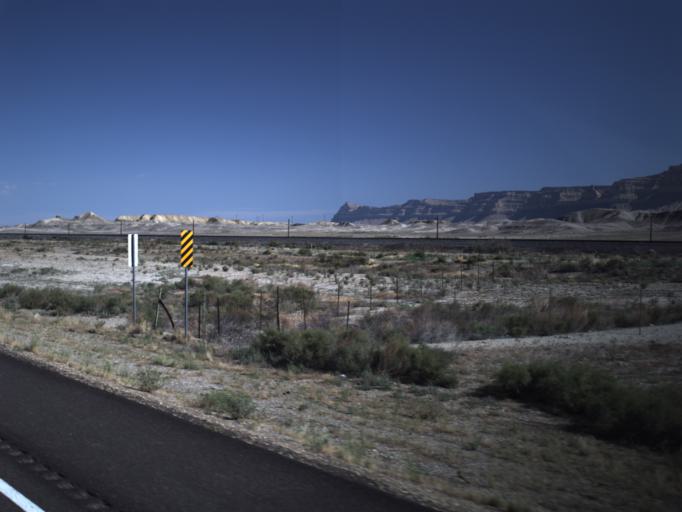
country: US
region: Utah
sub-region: Carbon County
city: East Carbon City
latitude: 39.0104
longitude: -110.2819
